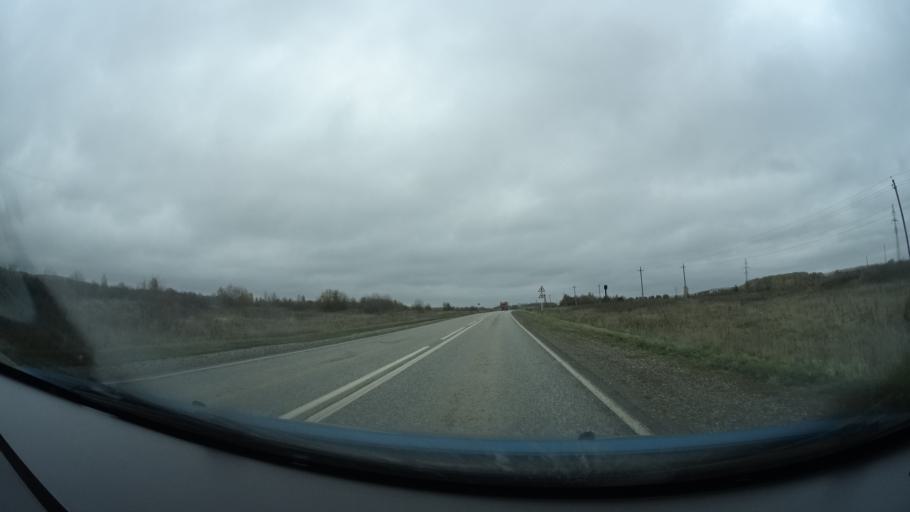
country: RU
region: Perm
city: Barda
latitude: 57.0850
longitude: 55.5409
